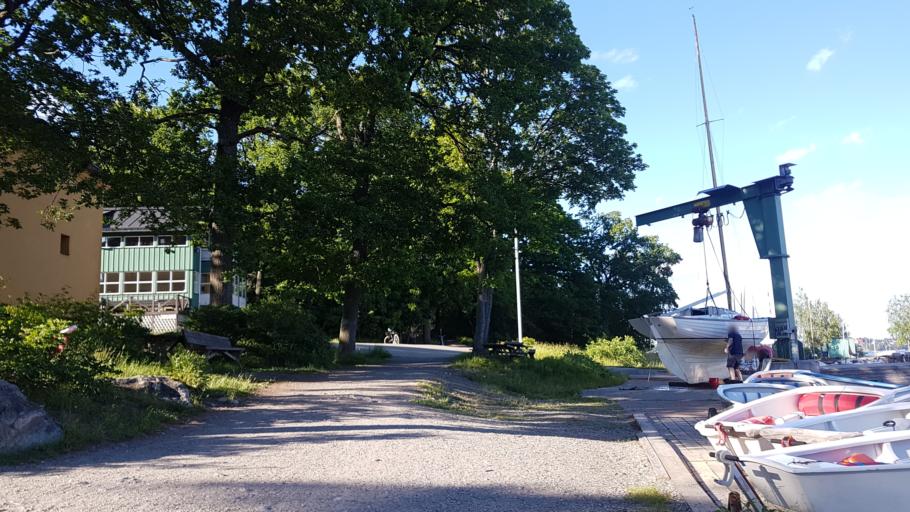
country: SE
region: Stockholm
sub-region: Nacka Kommun
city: Nacka
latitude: 59.3281
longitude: 18.1517
